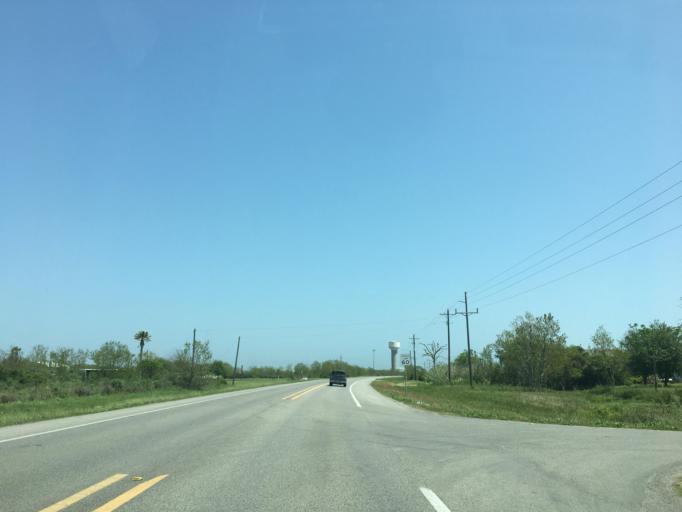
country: US
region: Texas
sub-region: Galveston County
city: Bolivar Peninsula
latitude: 29.4169
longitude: -94.7088
